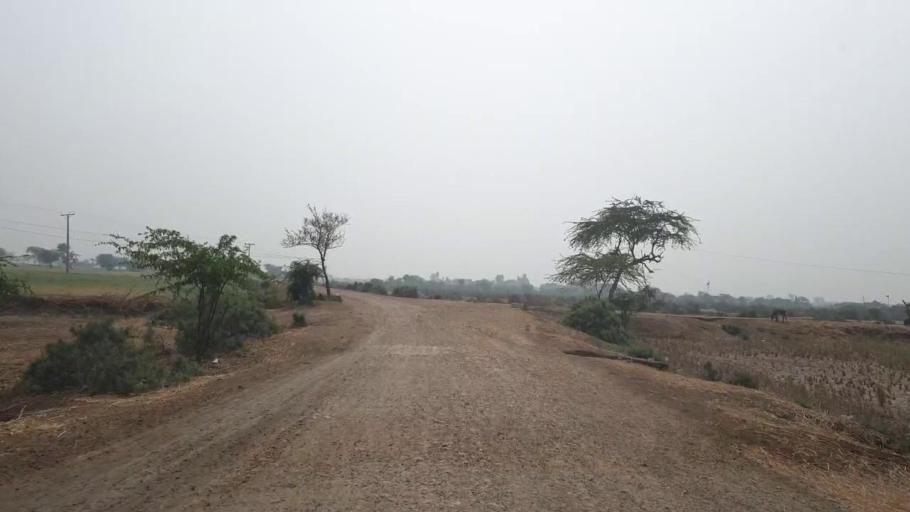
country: PK
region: Sindh
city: Kario
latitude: 24.6441
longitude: 68.6399
